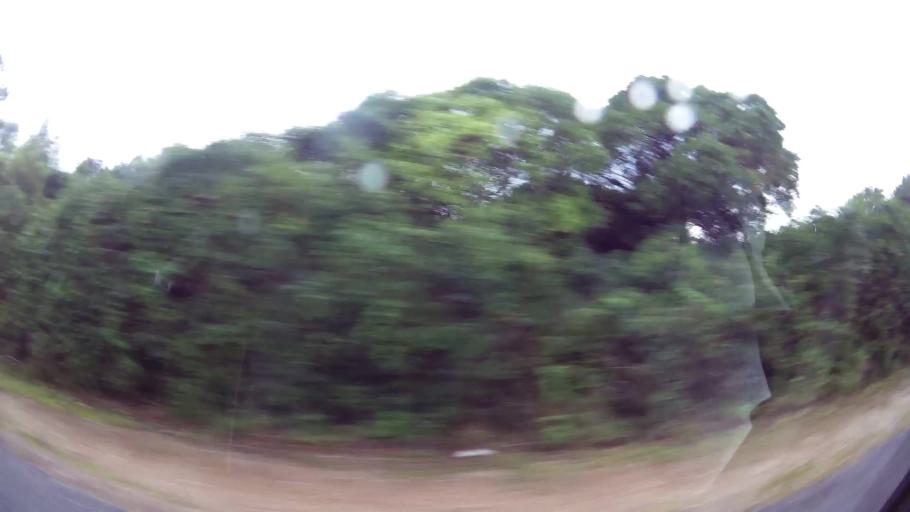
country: ZA
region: Eastern Cape
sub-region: Nelson Mandela Bay Metropolitan Municipality
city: Port Elizabeth
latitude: -34.0162
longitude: 25.5090
